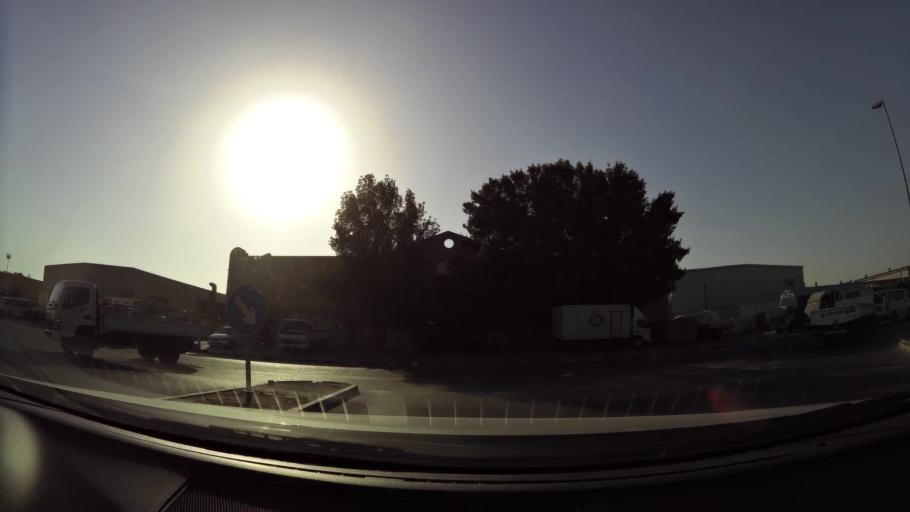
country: AE
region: Dubai
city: Dubai
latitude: 25.1337
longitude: 55.2485
